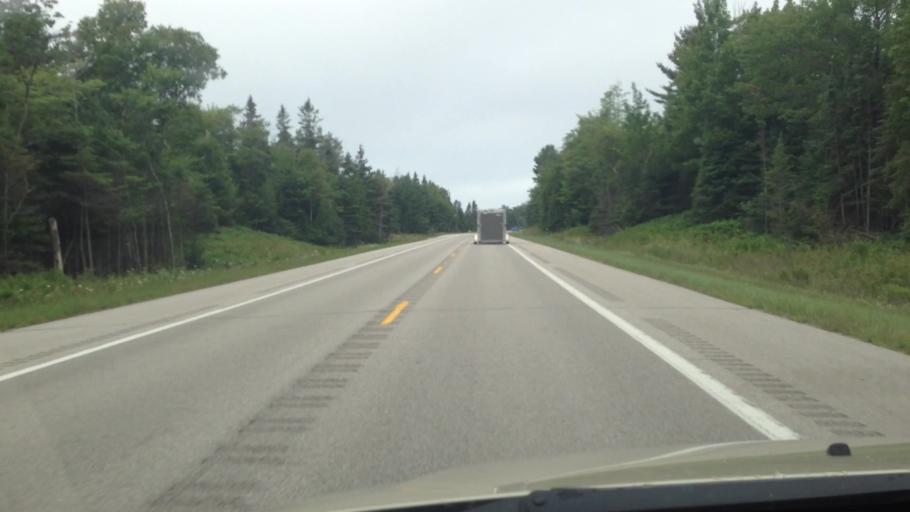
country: US
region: Michigan
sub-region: Luce County
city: Newberry
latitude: 46.0656
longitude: -85.2456
